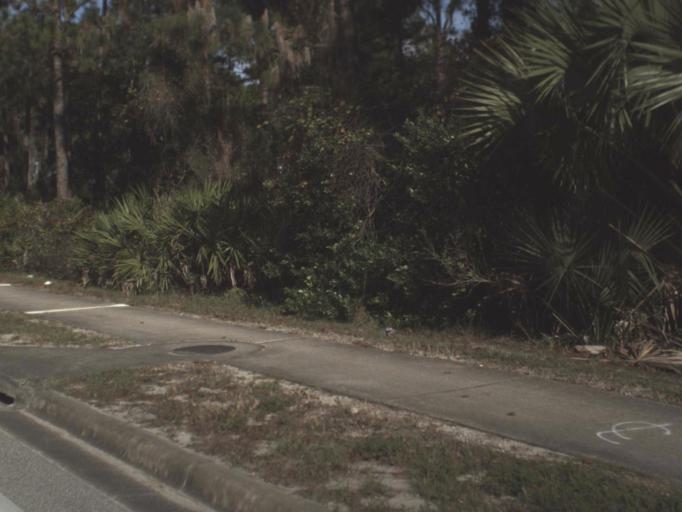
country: US
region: Florida
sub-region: Volusia County
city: South Daytona
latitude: 29.1414
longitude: -81.0352
